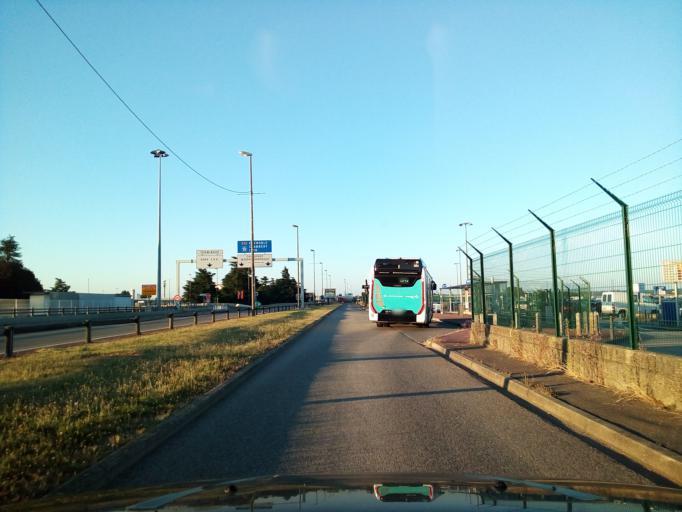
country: FR
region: Rhone-Alpes
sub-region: Departement du Rhone
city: Pusignan
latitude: 45.7212
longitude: 5.0696
